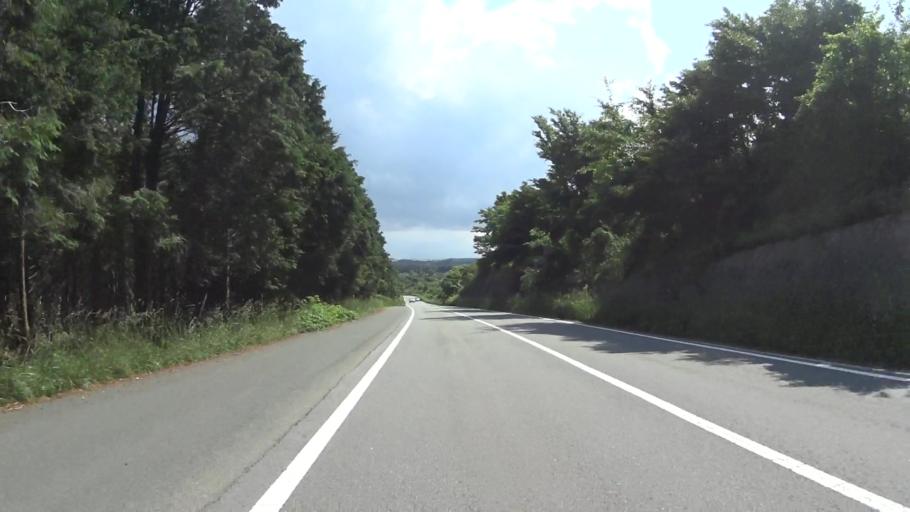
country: JP
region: Kumamoto
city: Aso
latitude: 33.0491
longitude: 131.1687
